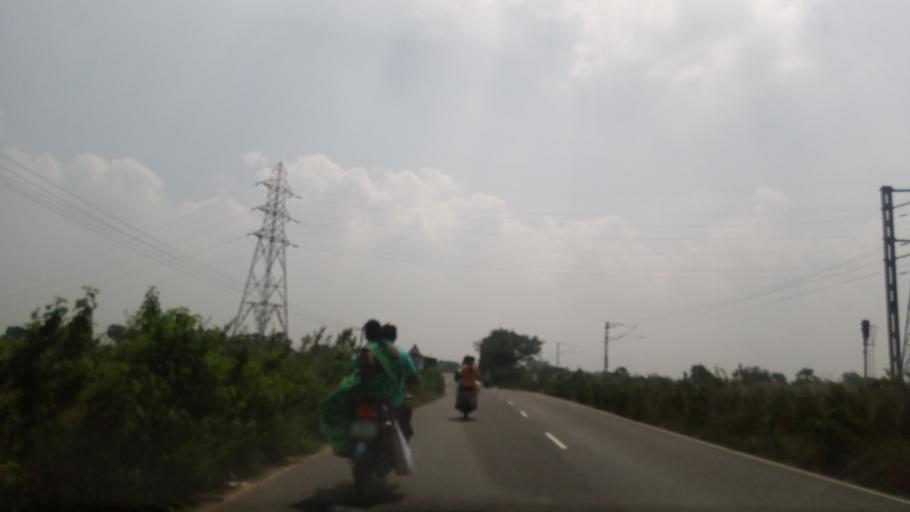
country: IN
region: Tamil Nadu
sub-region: Kancheepuram
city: Kanchipuram
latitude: 12.8876
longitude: 79.6874
